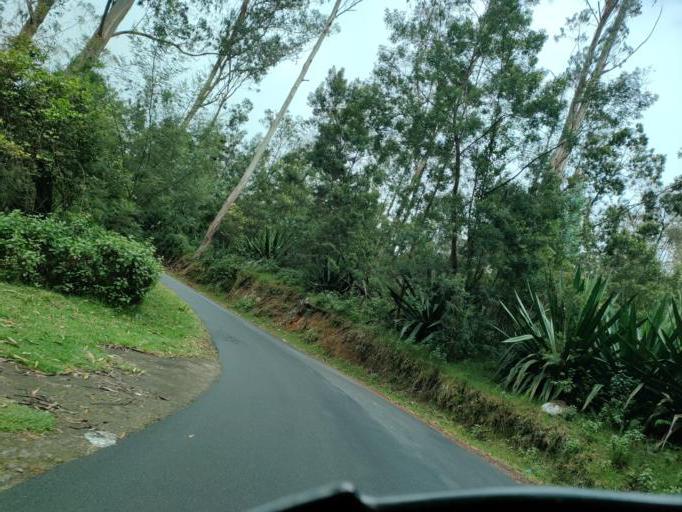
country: IN
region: Tamil Nadu
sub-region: Dindigul
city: Kodaikanal
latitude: 10.2435
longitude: 77.3703
